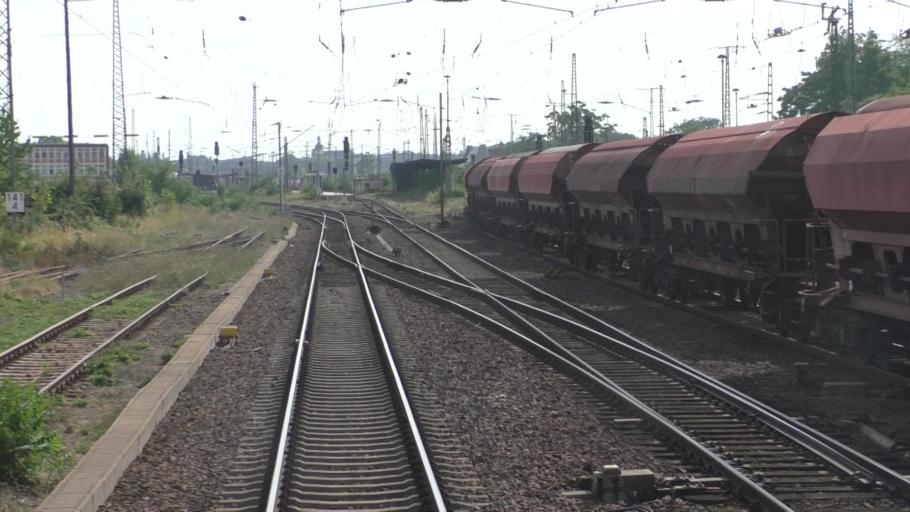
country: DE
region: Saxony-Anhalt
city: Magdeburg
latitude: 52.1351
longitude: 11.6280
